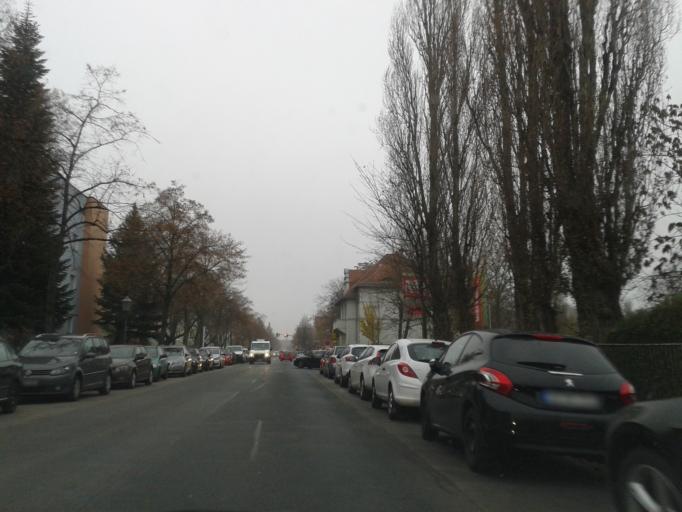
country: DE
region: Saxony
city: Radebeul
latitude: 51.0904
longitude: 13.7065
